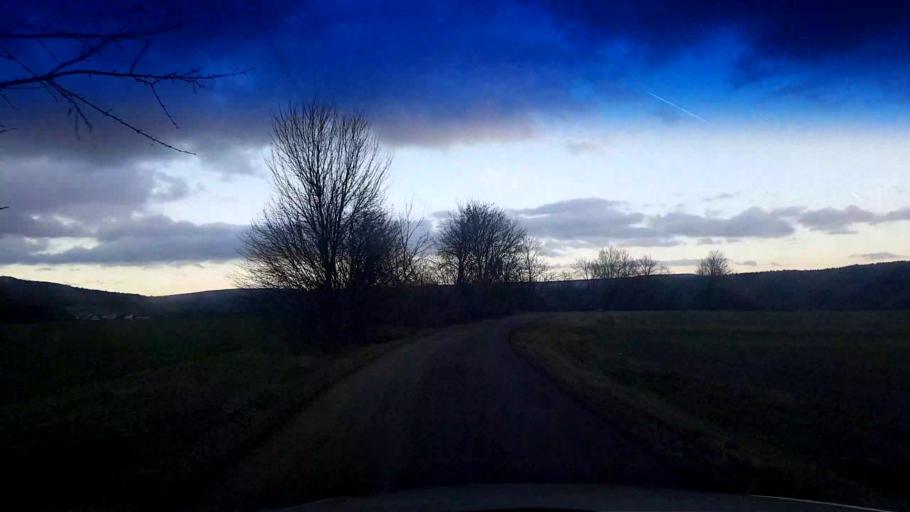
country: DE
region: Bavaria
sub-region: Upper Franconia
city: Buttenheim
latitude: 49.8134
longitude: 11.0526
